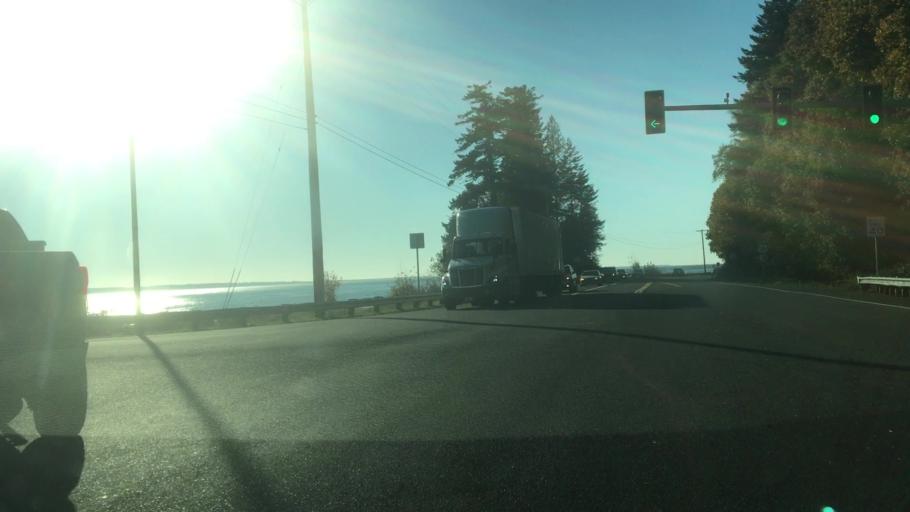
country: US
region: Oregon
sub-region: Clatsop County
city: Astoria
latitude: 46.2412
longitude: -123.8748
